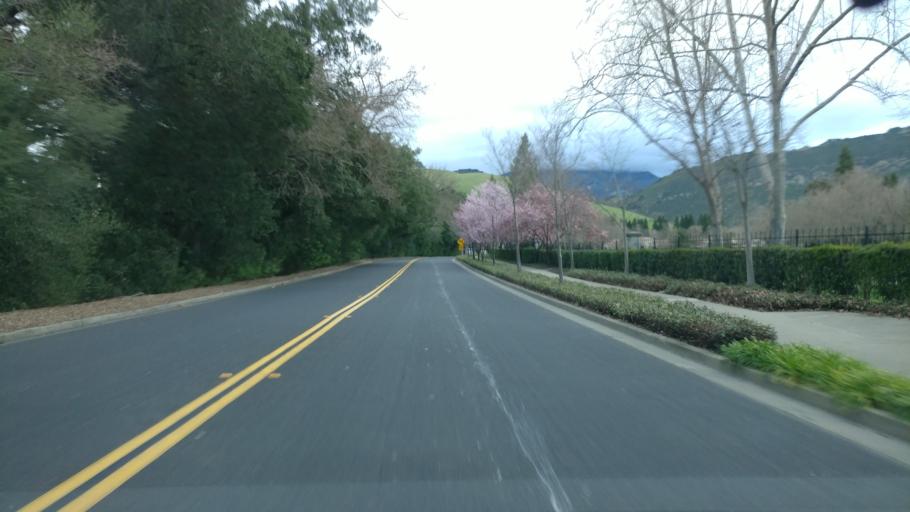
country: US
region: California
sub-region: Contra Costa County
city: Blackhawk
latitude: 37.8191
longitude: -121.9209
